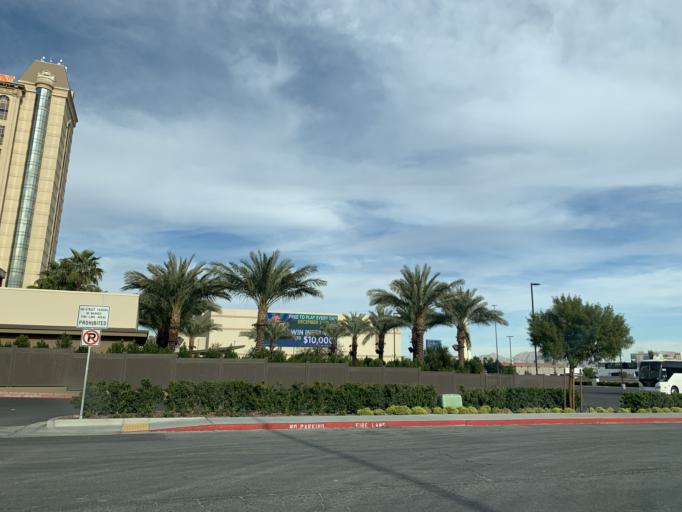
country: US
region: Nevada
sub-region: Clark County
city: Las Vegas
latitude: 36.1410
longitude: -115.1759
